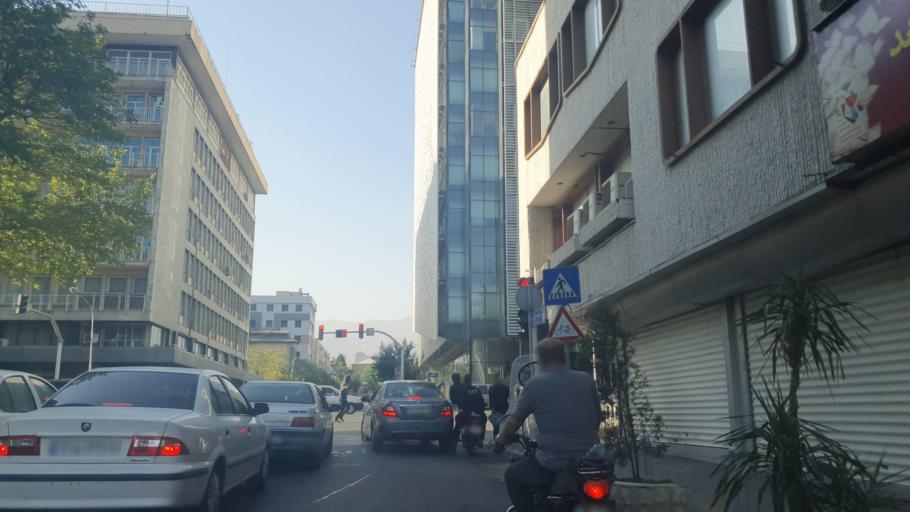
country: IR
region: Tehran
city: Tehran
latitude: 35.7065
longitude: 51.4210
